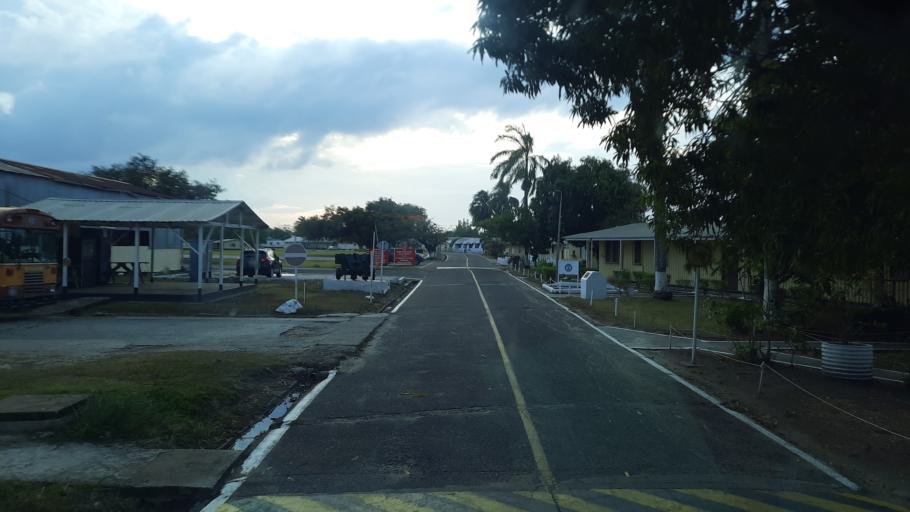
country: BZ
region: Belize
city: Belize City
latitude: 17.5430
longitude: -88.3036
